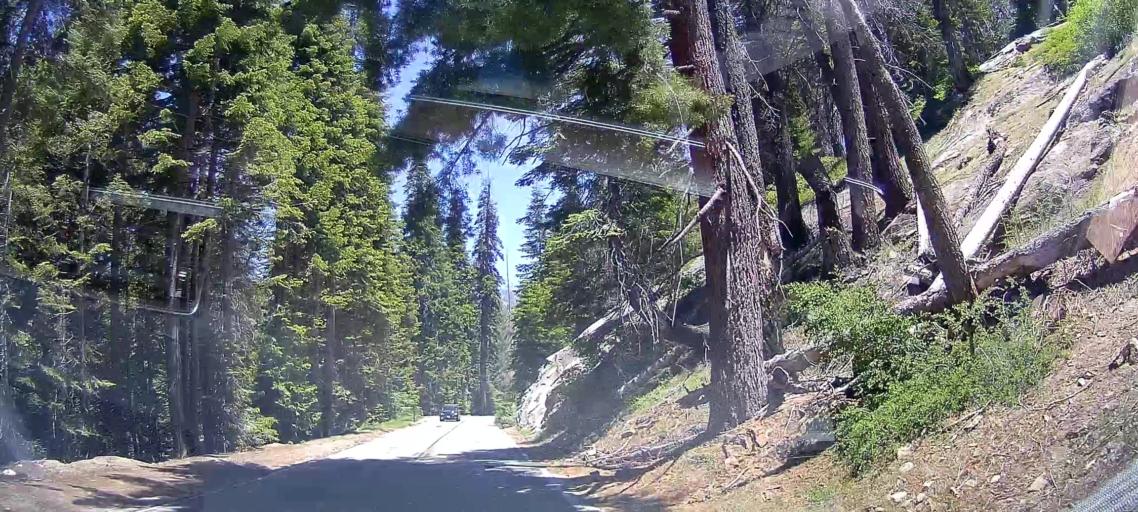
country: US
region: California
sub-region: Tulare County
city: Three Rivers
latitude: 36.6282
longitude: -118.8054
